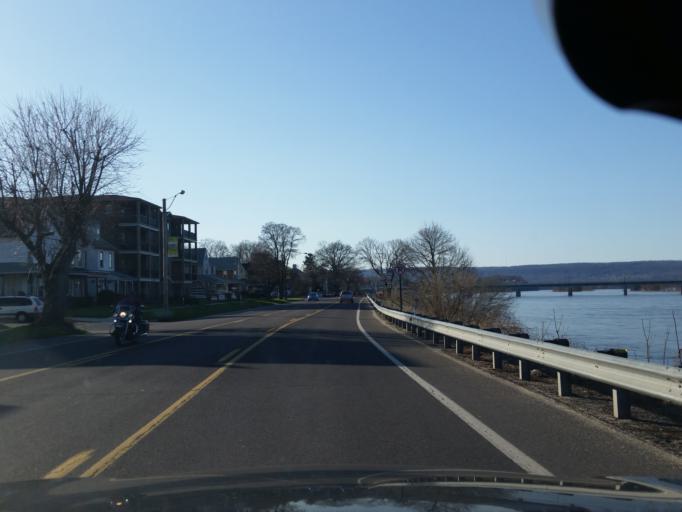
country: US
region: Pennsylvania
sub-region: Cumberland County
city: Lemoyne
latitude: 40.2548
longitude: -76.8984
